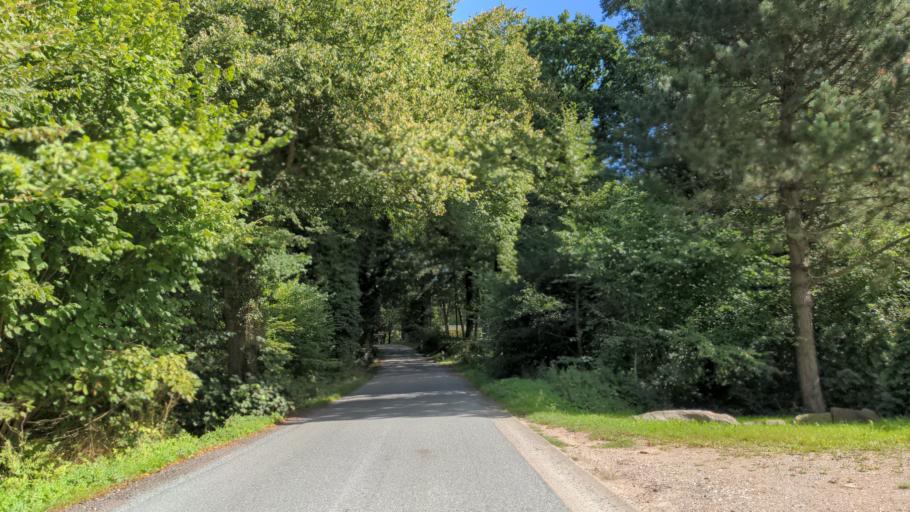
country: DE
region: Schleswig-Holstein
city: Kasseedorf
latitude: 54.1558
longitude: 10.7216
